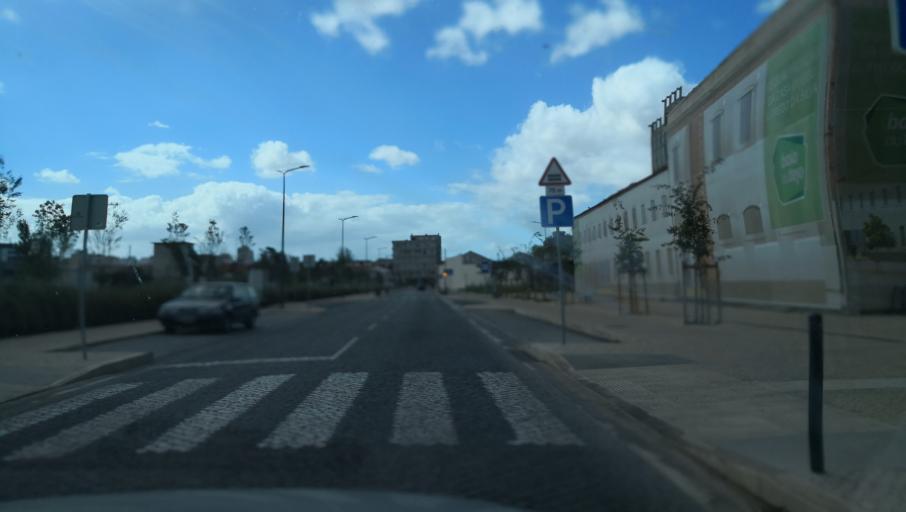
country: PT
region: Setubal
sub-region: Barreiro
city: Barreiro
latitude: 38.6661
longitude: -9.0714
